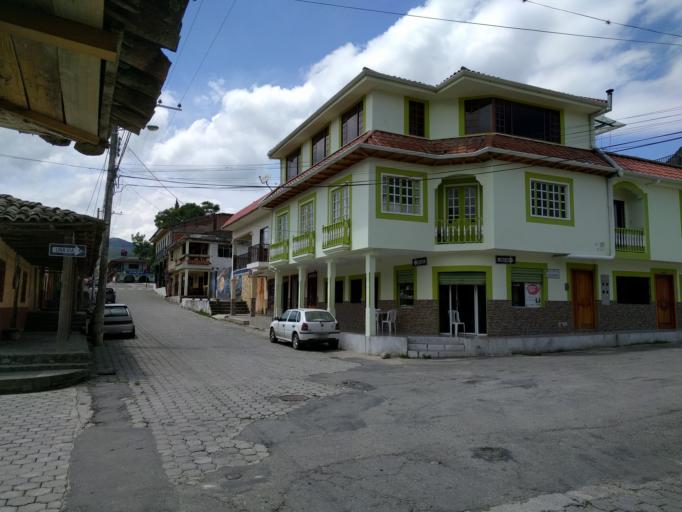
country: EC
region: Loja
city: Loja
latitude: -4.2598
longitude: -79.2221
